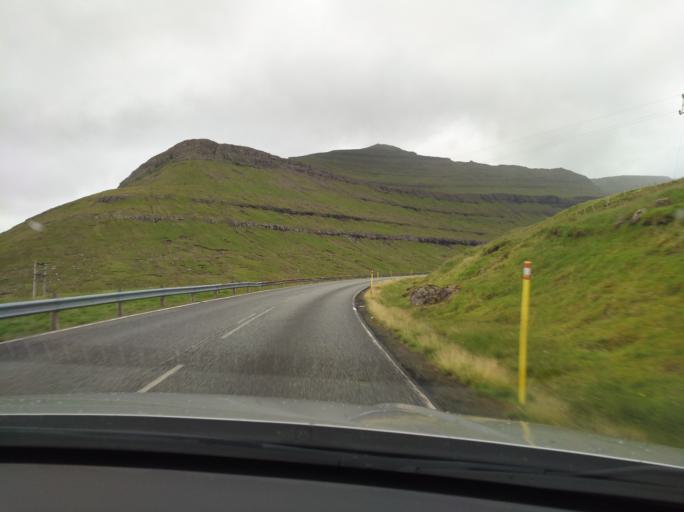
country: FO
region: Eysturoy
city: Fuglafjordur
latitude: 62.2232
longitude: -6.8786
